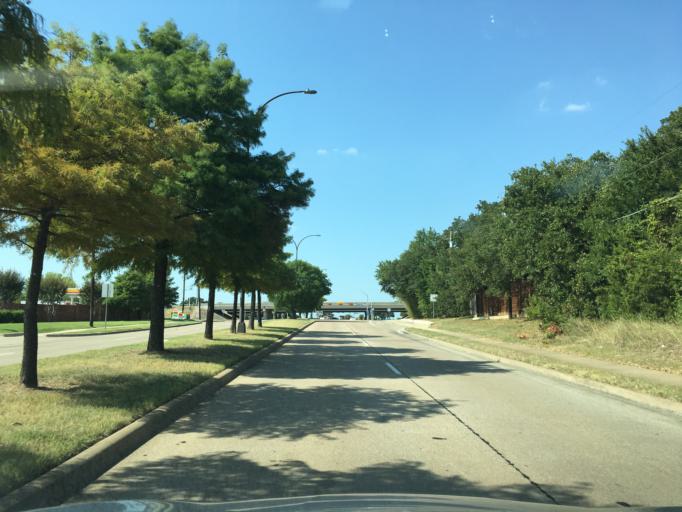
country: US
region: Texas
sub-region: Tarrant County
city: Dalworthington Gardens
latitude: 32.6723
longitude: -97.1496
